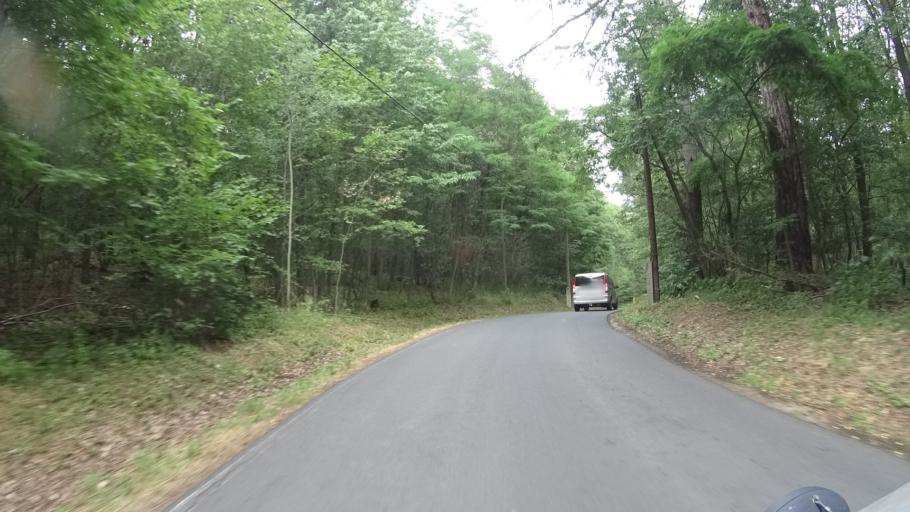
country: CZ
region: Ustecky
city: Zitenice
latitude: 50.5726
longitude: 14.1228
